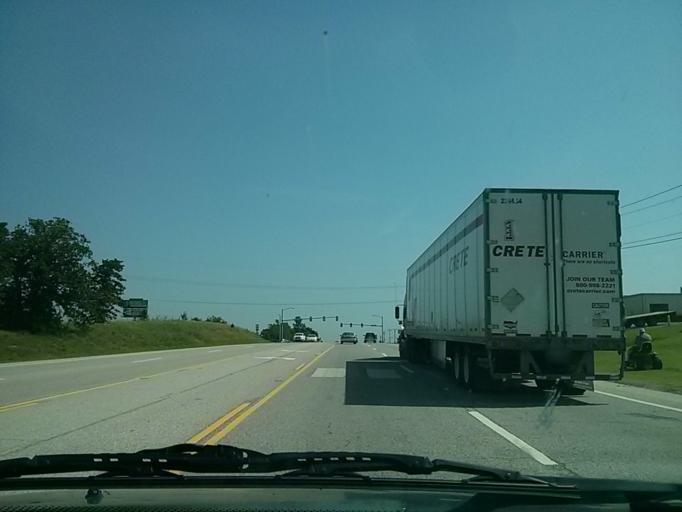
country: US
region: Oklahoma
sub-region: Tulsa County
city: Oakhurst
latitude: 36.0449
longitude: -96.0793
